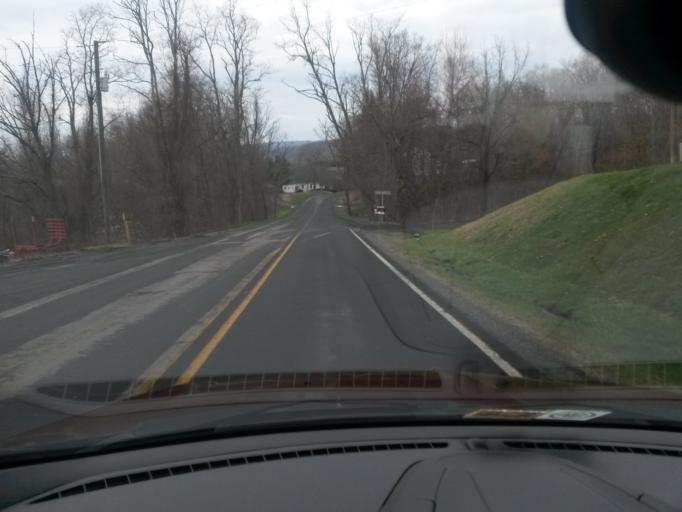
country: US
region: Virginia
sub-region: Bath County
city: Warm Springs
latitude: 38.0776
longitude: -79.7816
